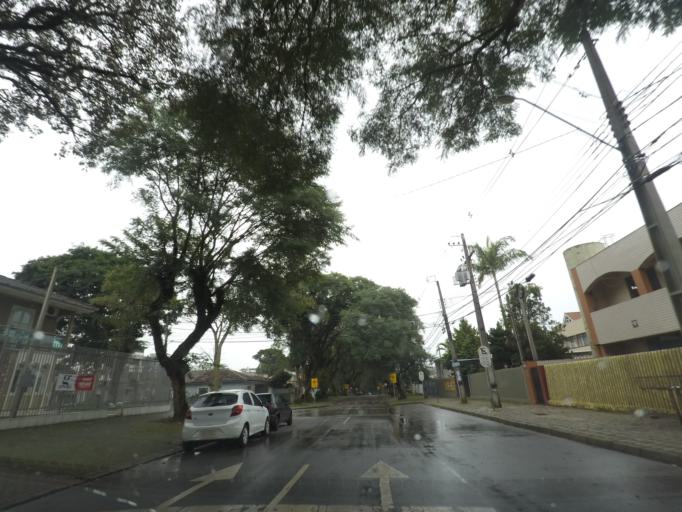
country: BR
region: Parana
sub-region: Curitiba
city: Curitiba
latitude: -25.4758
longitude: -49.3013
